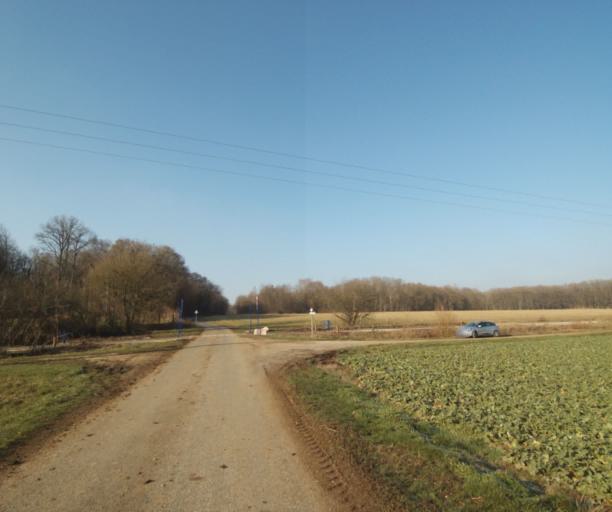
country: FR
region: Champagne-Ardenne
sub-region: Departement de la Haute-Marne
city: Wassy
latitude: 48.4515
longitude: 4.9491
